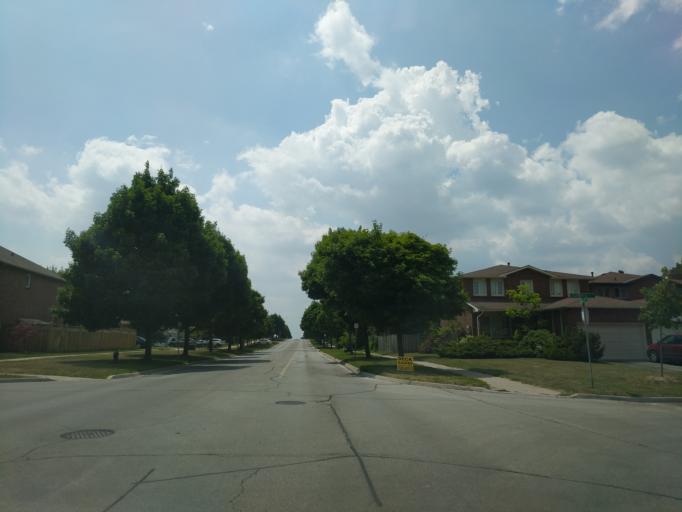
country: CA
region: Ontario
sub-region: York
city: Richmond Hill
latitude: 43.8679
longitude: -79.4179
